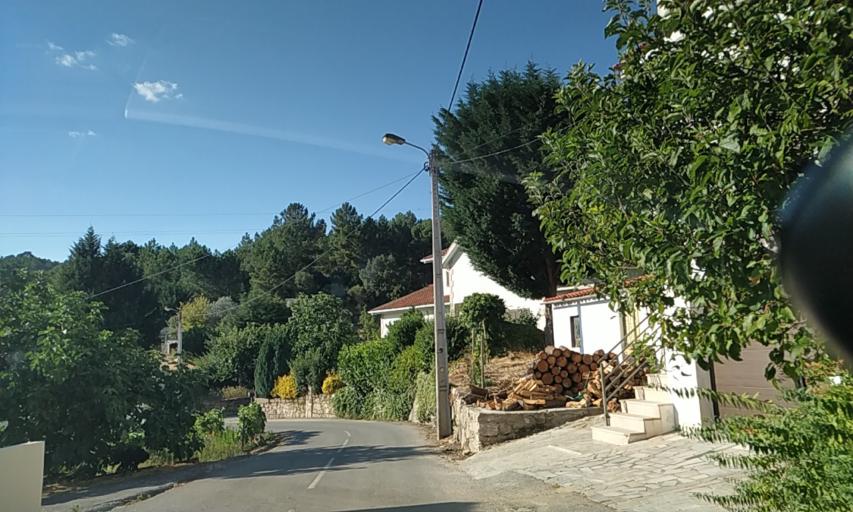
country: PT
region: Viseu
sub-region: Sao Joao da Pesqueira
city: Sao Joao da Pesqueira
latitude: 41.2532
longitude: -7.4271
